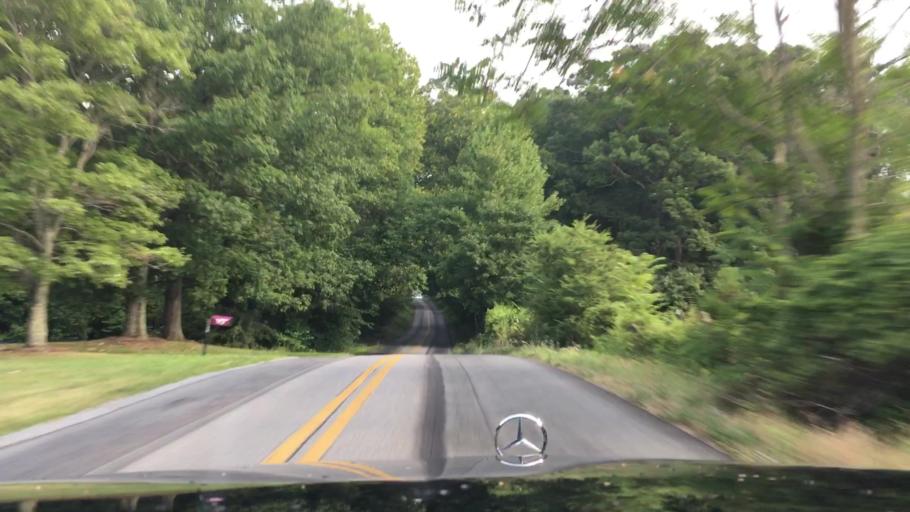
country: US
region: Virginia
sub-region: Campbell County
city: Timberlake
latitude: 37.2738
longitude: -79.3122
